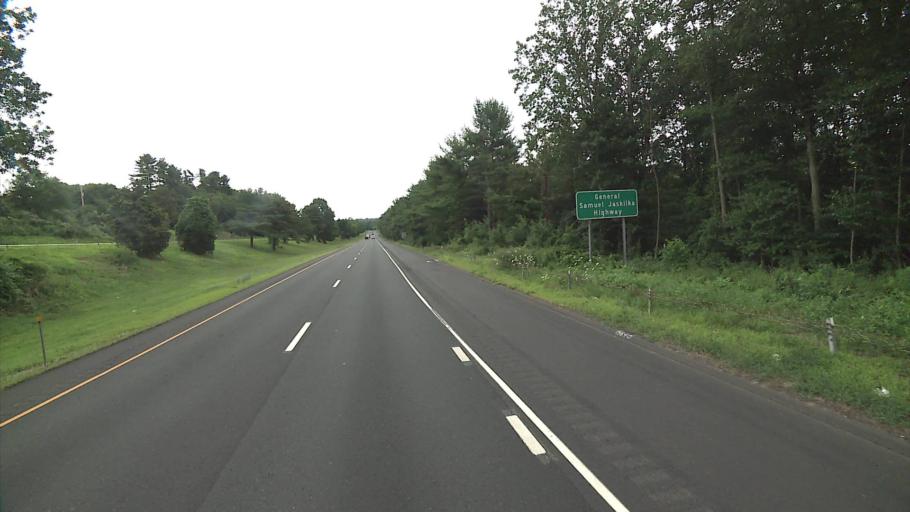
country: US
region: Connecticut
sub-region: Fairfield County
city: Trumbull
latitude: 41.2584
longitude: -73.1413
